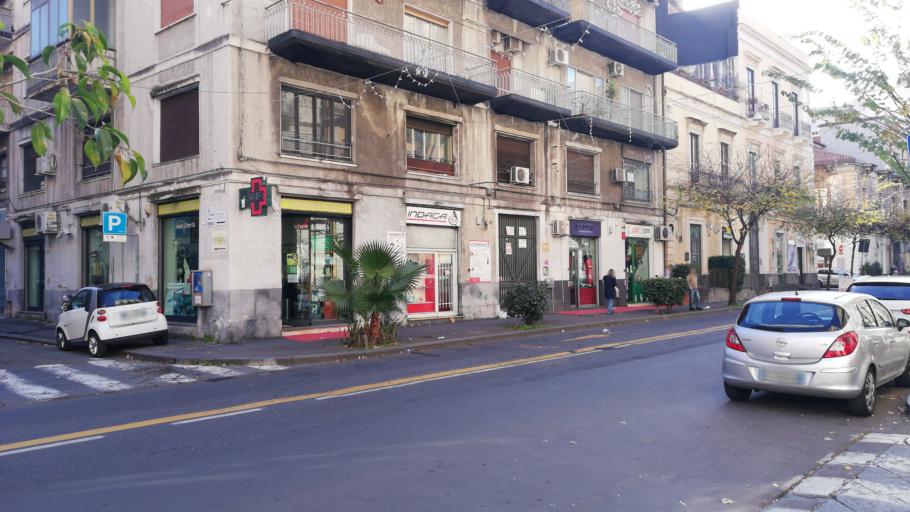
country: IT
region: Sicily
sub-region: Catania
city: Canalicchio
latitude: 37.5141
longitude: 15.0977
